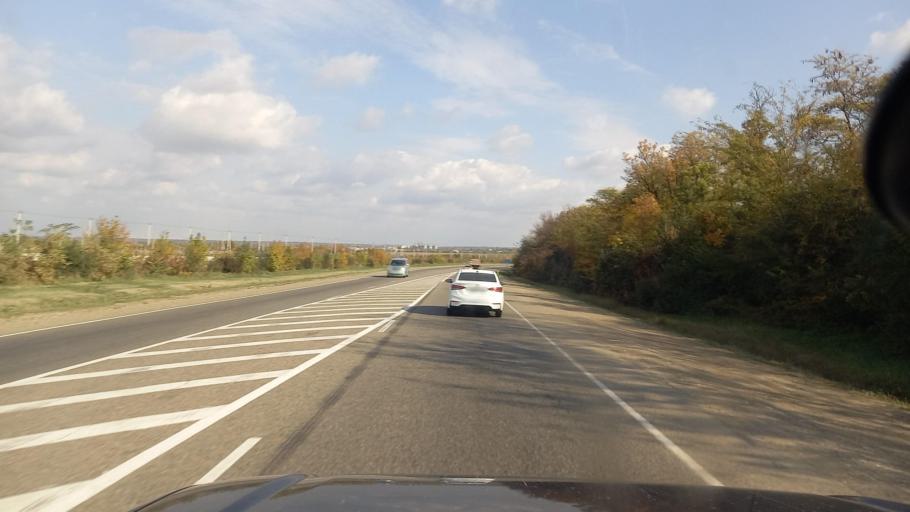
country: RU
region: Krasnodarskiy
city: Akhtyrskiy
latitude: 44.8492
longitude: 38.3155
